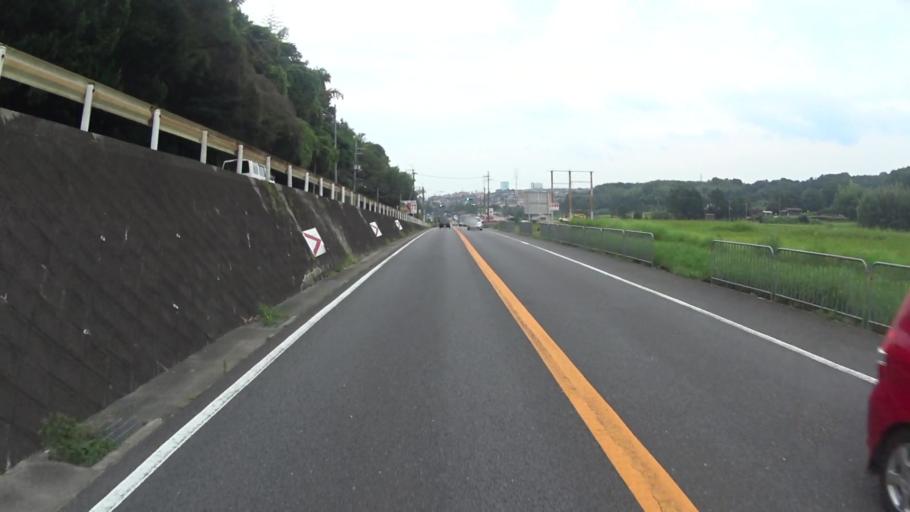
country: JP
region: Nara
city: Nara-shi
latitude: 34.7310
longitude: 135.7632
